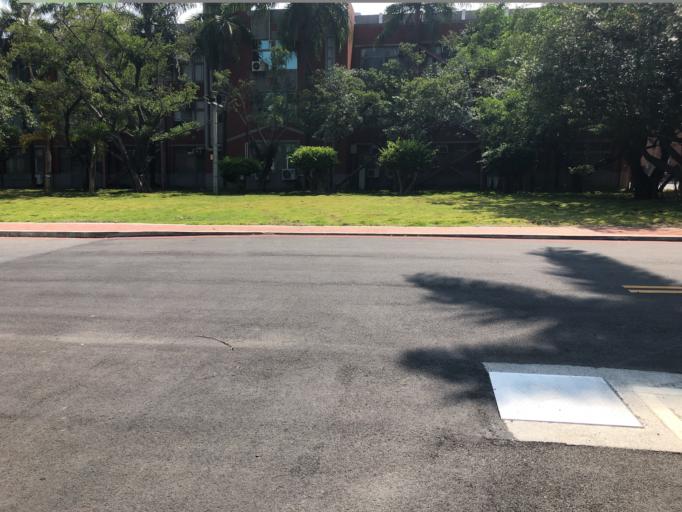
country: TW
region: Taiwan
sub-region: Tainan
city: Tainan
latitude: 23.0257
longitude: 120.2230
